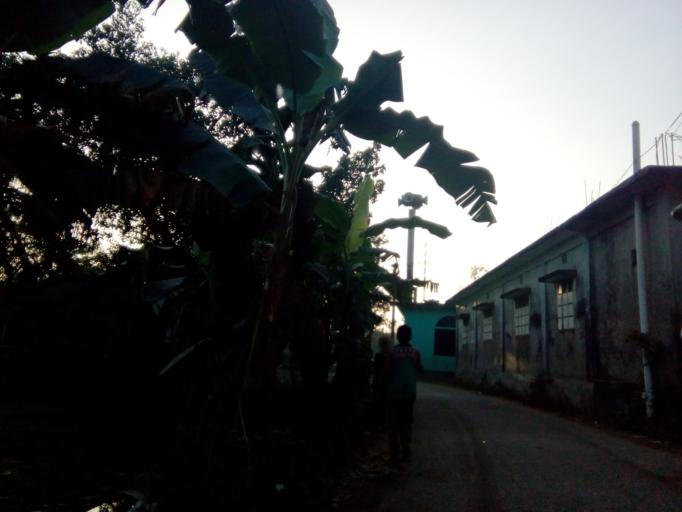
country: BD
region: Chittagong
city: Comilla
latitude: 23.4049
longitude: 91.1950
